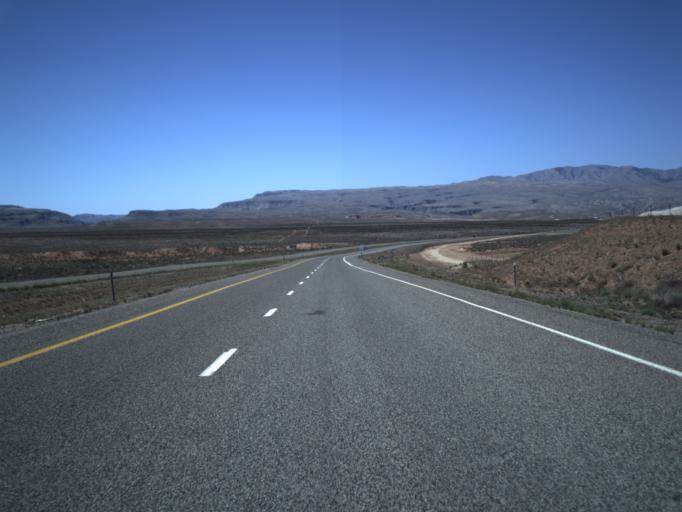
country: US
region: Utah
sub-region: Washington County
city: Saint George
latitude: 37.0008
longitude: -113.5670
